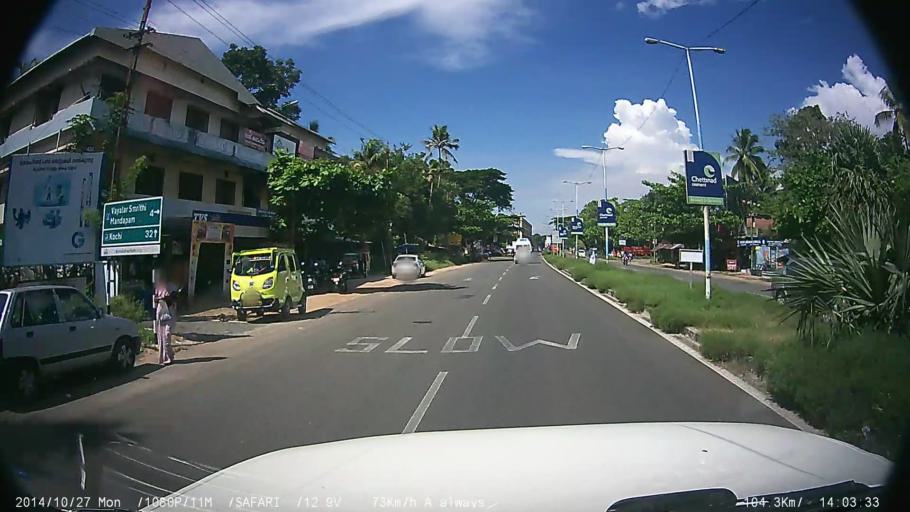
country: IN
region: Kerala
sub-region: Alappuzha
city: Vayalar
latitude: 9.7229
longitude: 76.3180
